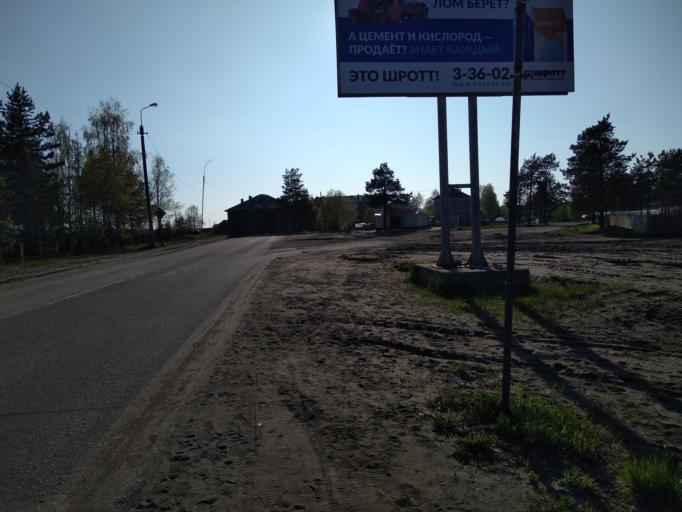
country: RU
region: Komi Republic
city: Puteyets
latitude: 65.1093
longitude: 57.1427
